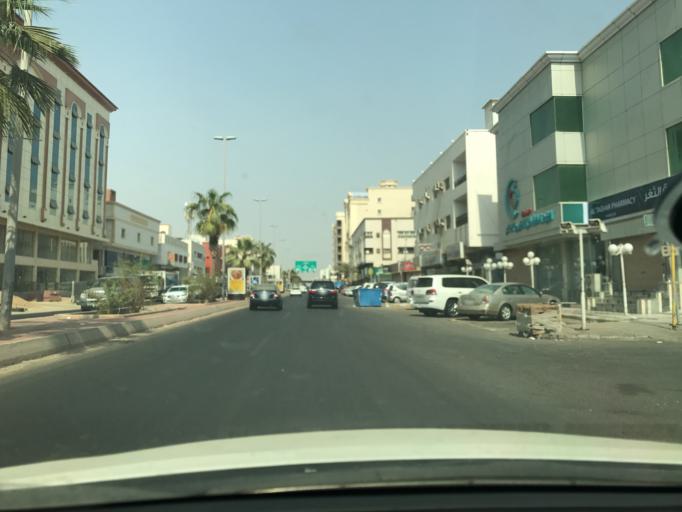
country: SA
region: Makkah
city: Jeddah
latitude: 21.6151
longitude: 39.1622
